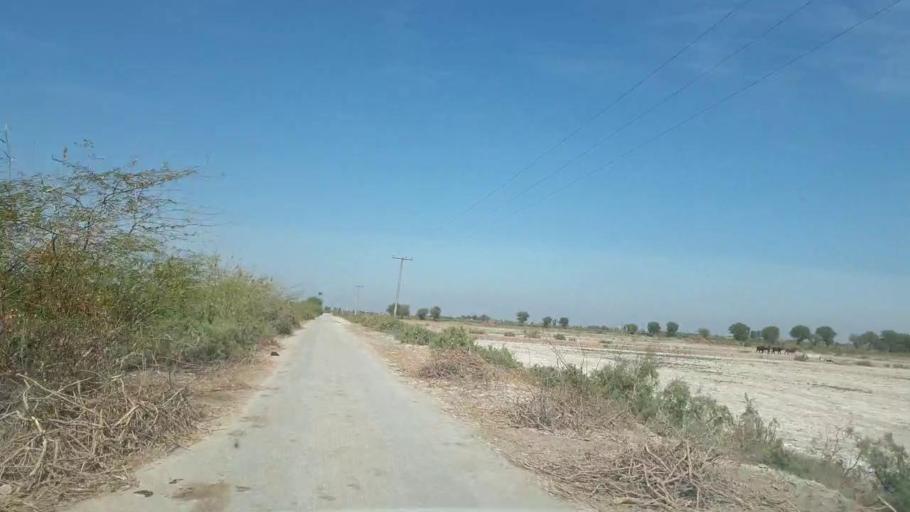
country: PK
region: Sindh
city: Pithoro
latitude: 25.6184
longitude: 69.2159
